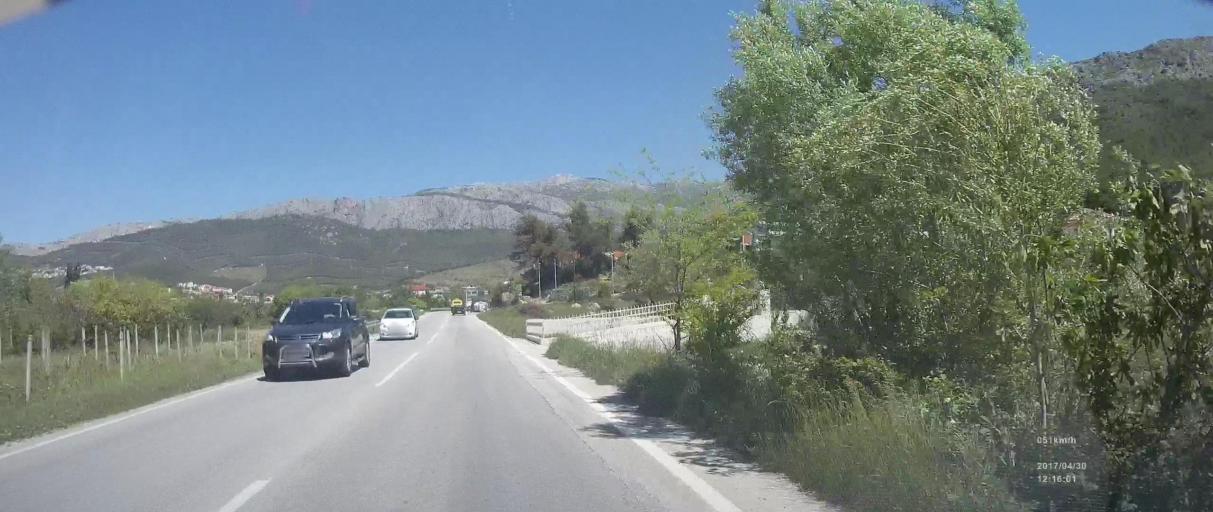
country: HR
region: Splitsko-Dalmatinska
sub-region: Grad Split
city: Stobrec
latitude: 43.5083
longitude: 16.5377
